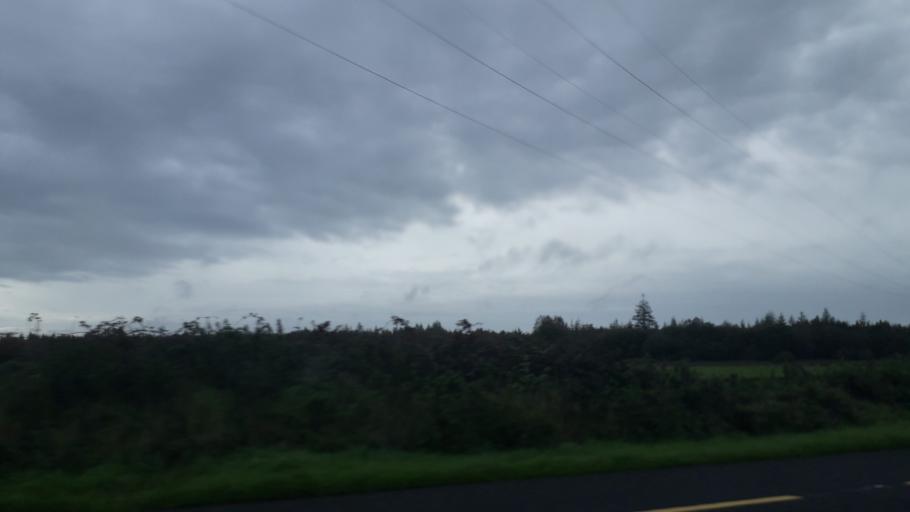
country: IE
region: Leinster
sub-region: An Longfort
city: Longford
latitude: 53.7271
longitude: -7.8833
